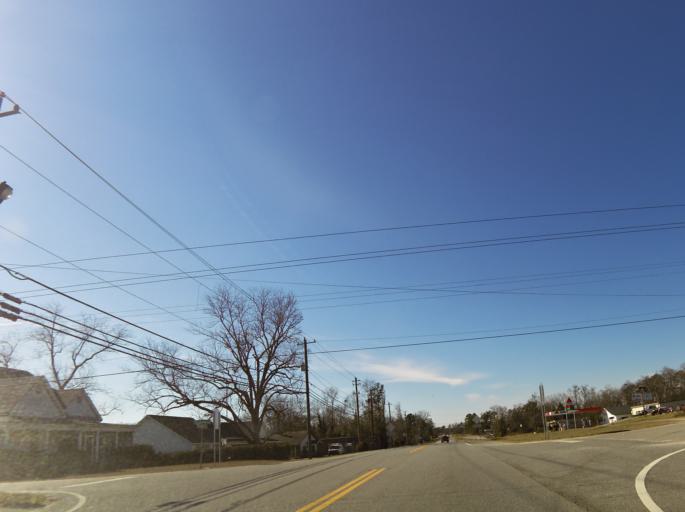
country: US
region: Georgia
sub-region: Bibb County
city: West Point
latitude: 32.8068
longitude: -83.8197
